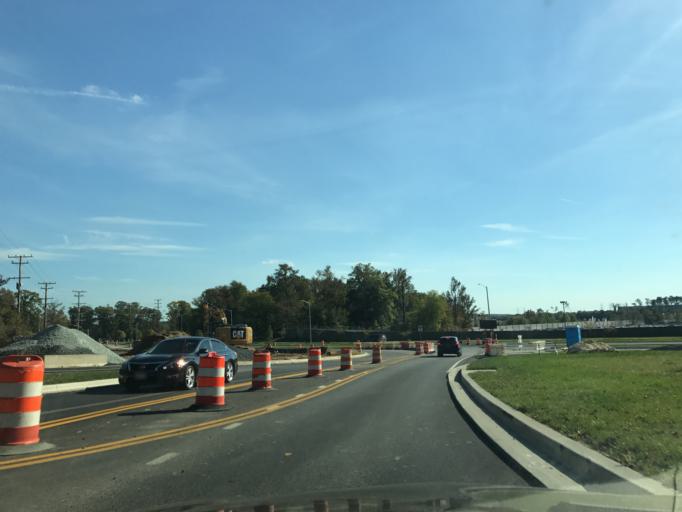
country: US
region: Maryland
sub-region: Prince George's County
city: West Laurel
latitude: 39.0815
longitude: -76.8817
